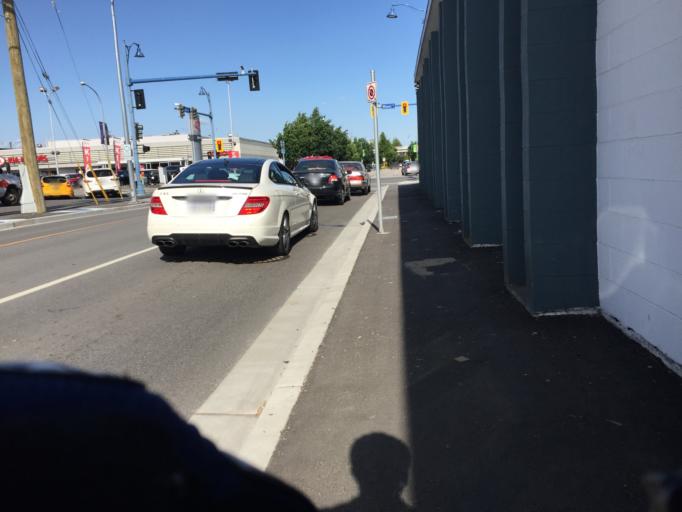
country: CA
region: British Columbia
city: Richmond
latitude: 49.1738
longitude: -123.1409
